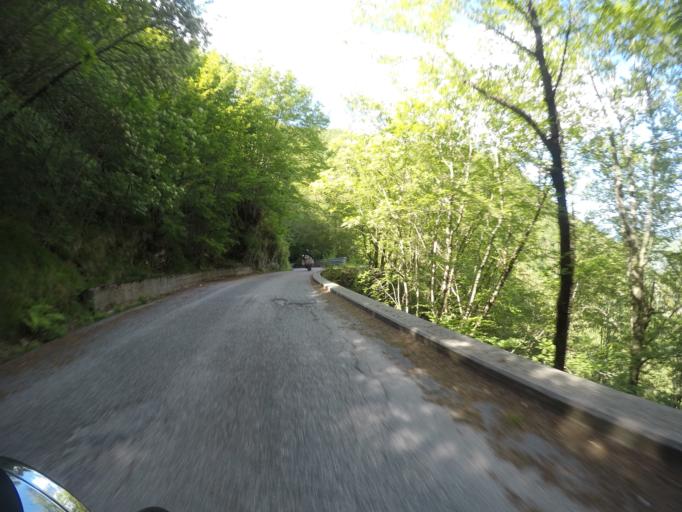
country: IT
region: Tuscany
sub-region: Provincia di Lucca
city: Minucciano
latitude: 44.1485
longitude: 10.1946
